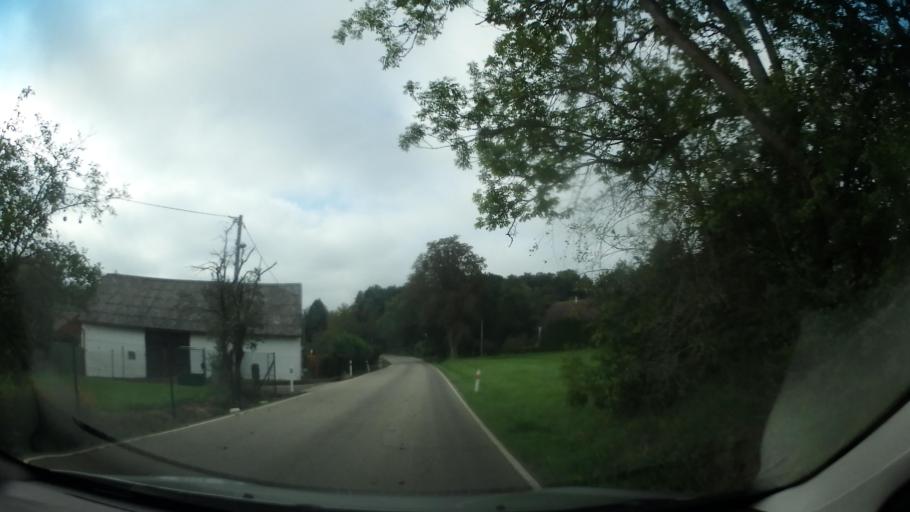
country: CZ
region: Central Bohemia
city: Neveklov
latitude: 49.7473
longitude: 14.5185
